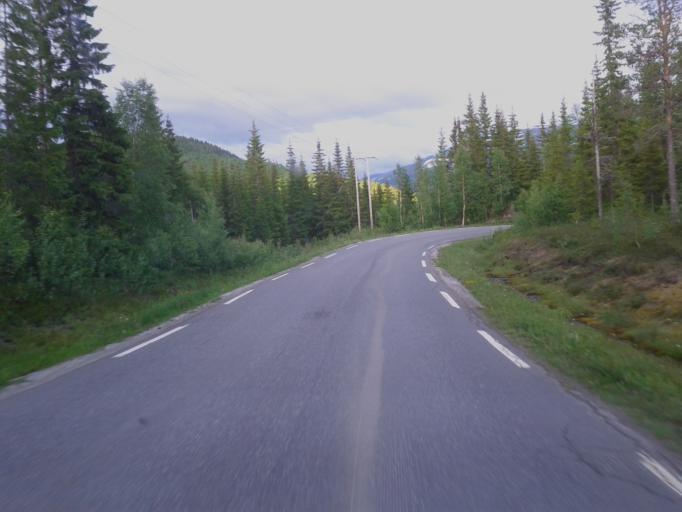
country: NO
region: Nordland
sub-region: Grane
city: Trofors
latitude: 65.5221
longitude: 13.6666
